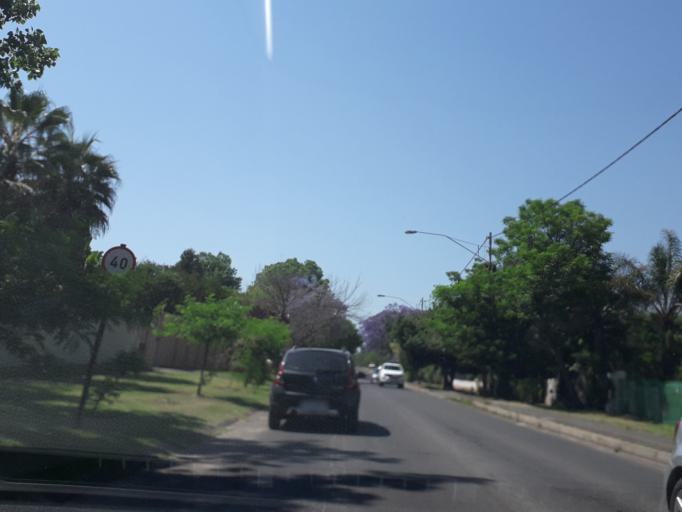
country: ZA
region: Gauteng
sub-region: City of Johannesburg Metropolitan Municipality
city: Johannesburg
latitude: -26.1273
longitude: 28.0222
